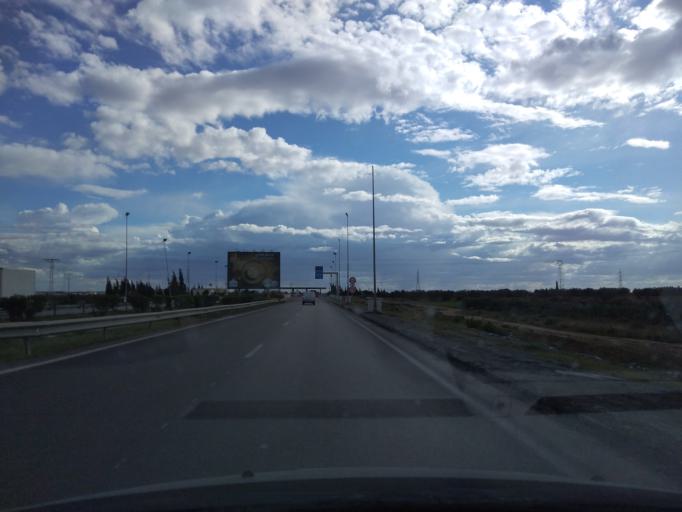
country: TN
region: Susah
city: Masakin
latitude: 35.6939
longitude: 10.5641
